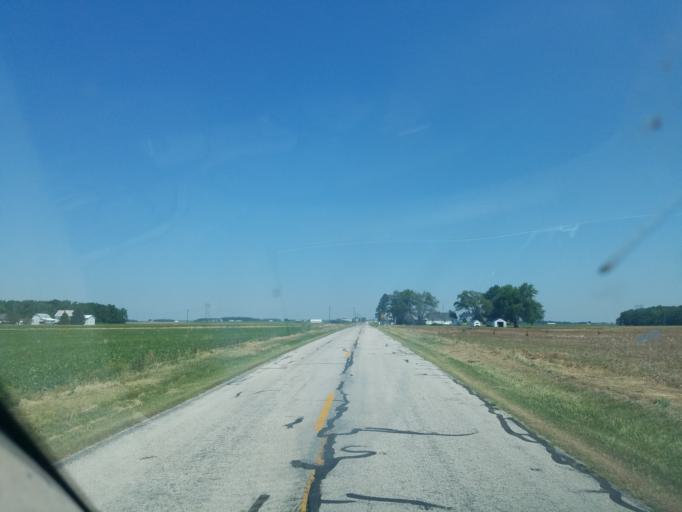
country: US
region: Ohio
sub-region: Mercer County
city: Rockford
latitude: 40.6087
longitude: -84.7085
